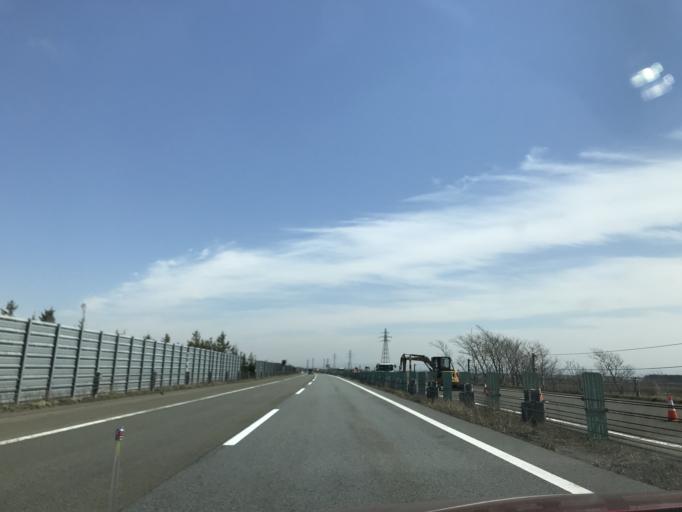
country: JP
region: Hokkaido
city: Ebetsu
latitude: 43.0830
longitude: 141.5552
